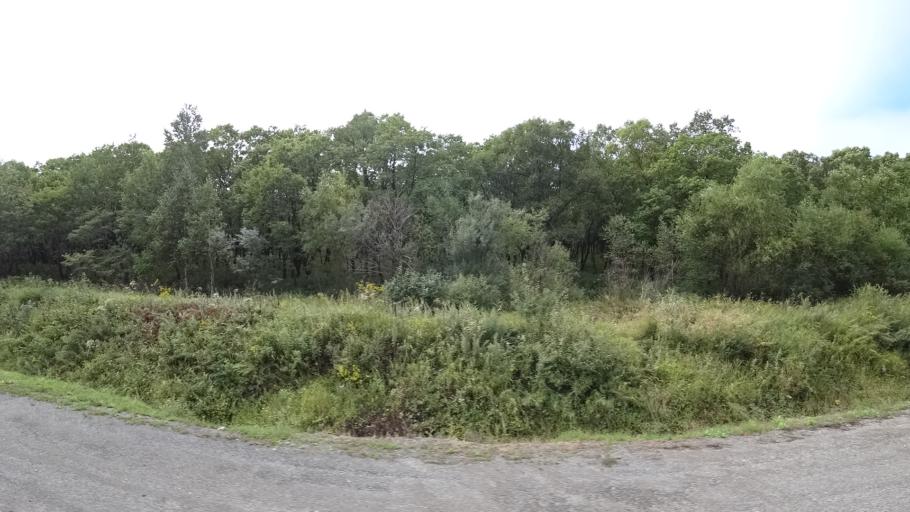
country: RU
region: Primorskiy
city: Lyalichi
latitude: 44.1013
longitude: 132.4241
